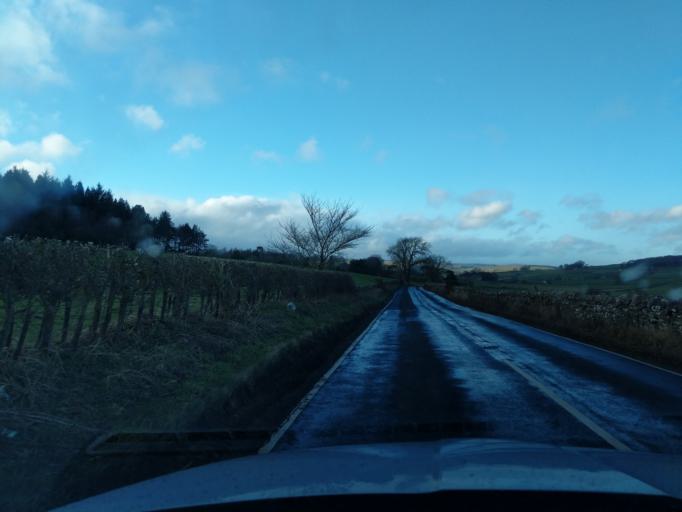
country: GB
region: England
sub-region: North Yorkshire
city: Leyburn
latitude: 54.3516
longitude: -1.8098
